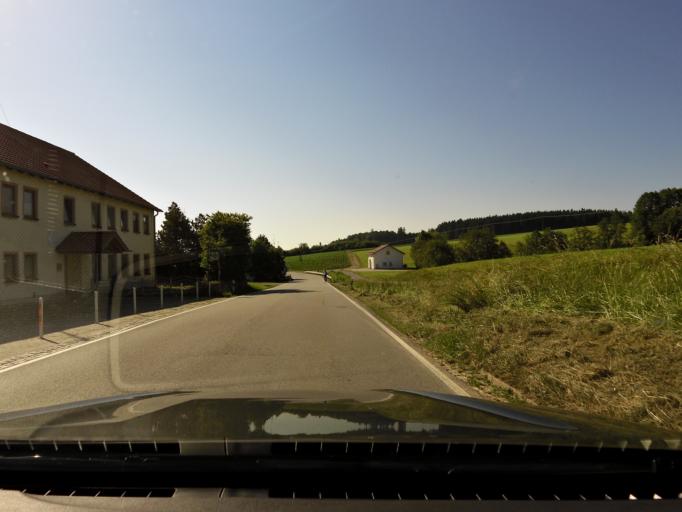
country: DE
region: Bavaria
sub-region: Upper Bavaria
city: Neumarkt-Sankt Veit
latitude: 48.3738
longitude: 12.4796
